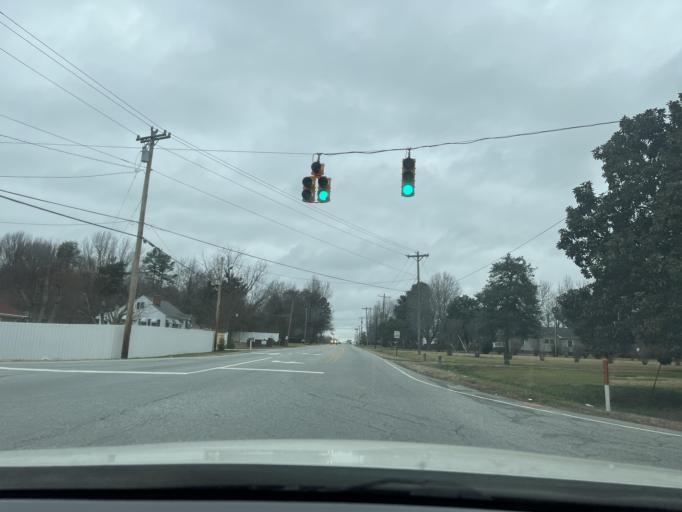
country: US
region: North Carolina
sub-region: Guilford County
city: Pleasant Garden
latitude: 35.9964
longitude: -79.8047
